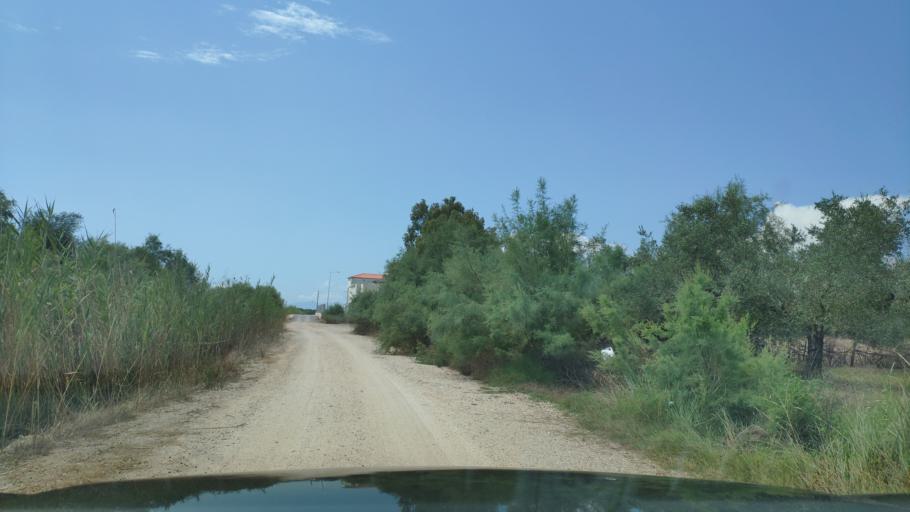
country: GR
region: West Greece
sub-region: Nomos Aitolias kai Akarnanias
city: Menidi
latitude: 39.0519
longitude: 21.1026
